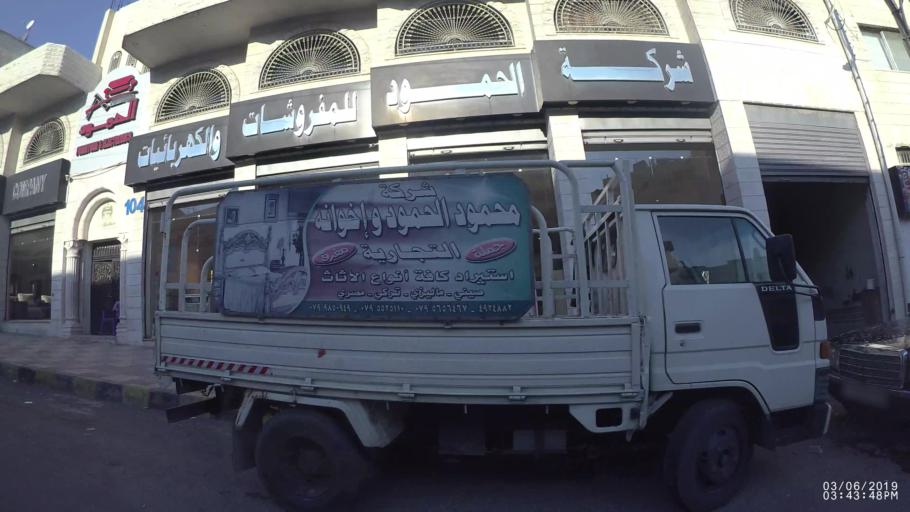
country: JO
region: Amman
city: Amman
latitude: 31.9685
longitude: 35.9605
